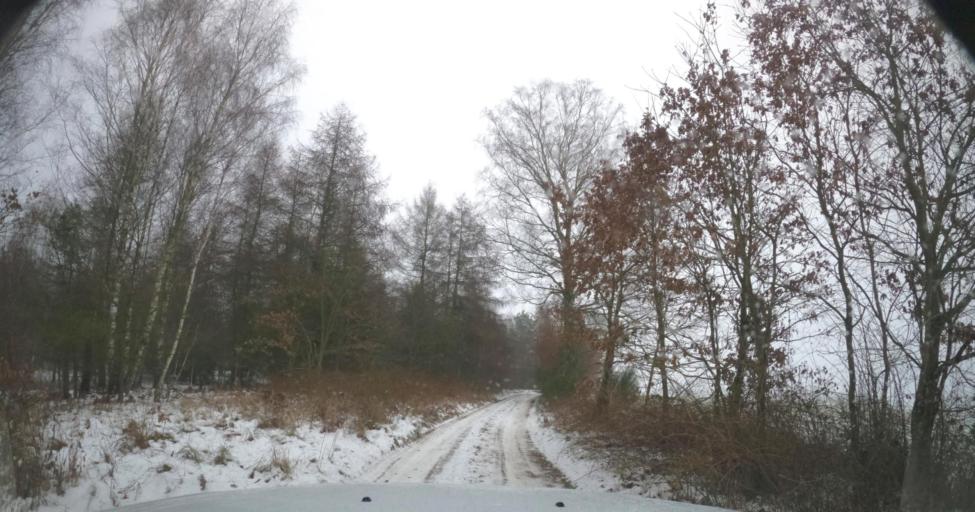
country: PL
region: West Pomeranian Voivodeship
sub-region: Powiat kamienski
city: Golczewo
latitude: 53.8710
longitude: 15.0552
